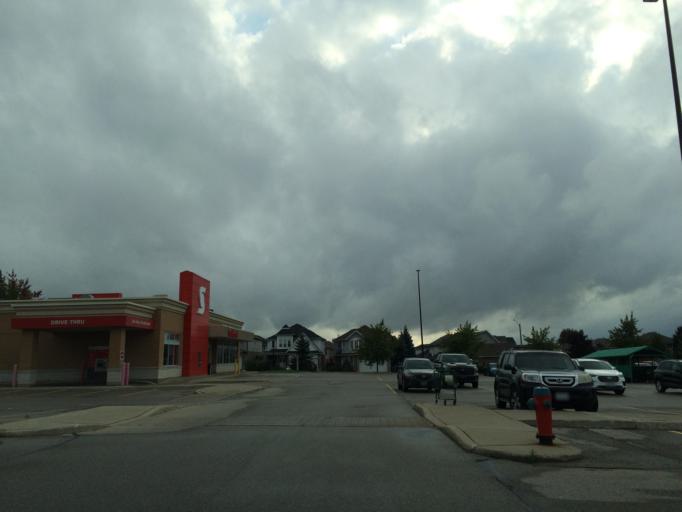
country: CA
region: Ontario
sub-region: Wellington County
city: Guelph
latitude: 43.4997
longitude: -80.1907
